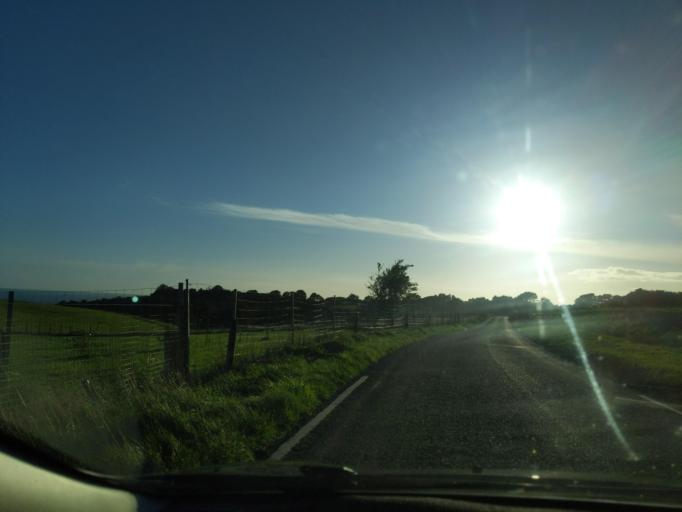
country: GB
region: England
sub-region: Plymouth
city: Plymstock
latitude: 50.3450
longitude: -4.1109
